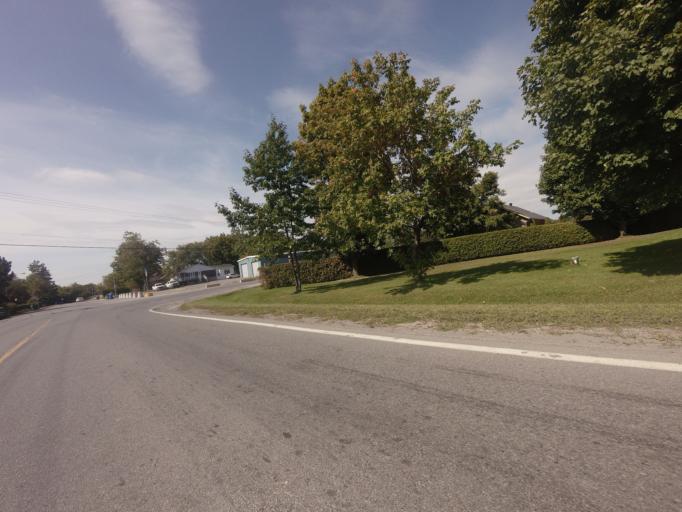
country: CA
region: Quebec
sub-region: Laurentides
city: Saint-Eustache
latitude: 45.5953
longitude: -73.9159
